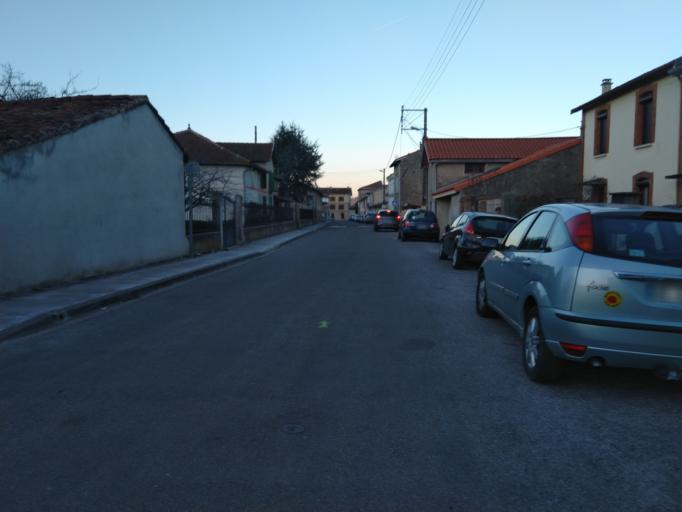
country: FR
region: Midi-Pyrenees
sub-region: Departement de l'Ariege
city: Pamiers
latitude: 43.1099
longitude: 1.6114
